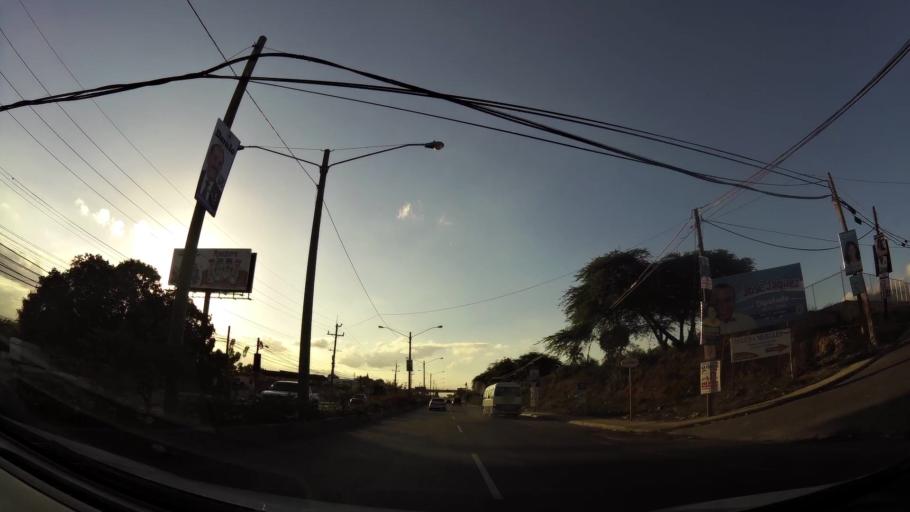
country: DO
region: Santiago
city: Palmar Arriba
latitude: 19.4975
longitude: -70.7375
